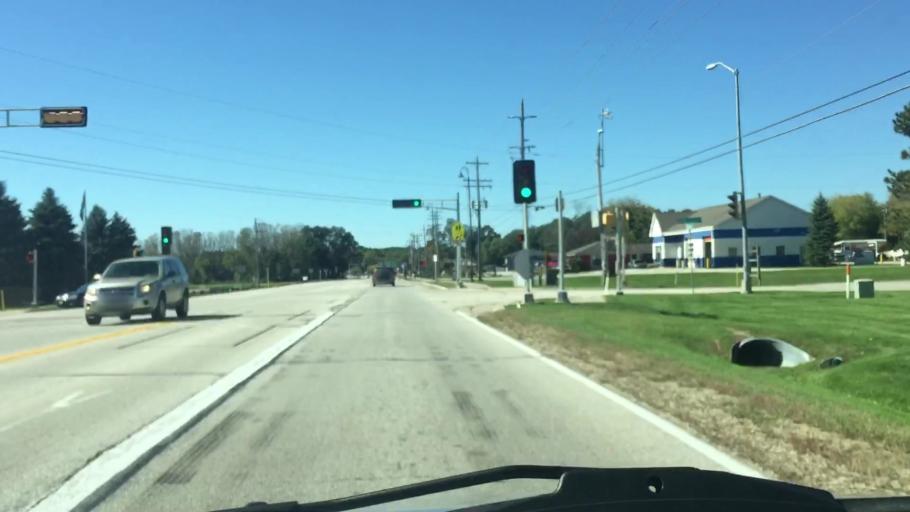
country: US
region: Wisconsin
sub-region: Waukesha County
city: Wales
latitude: 43.0138
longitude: -88.3777
